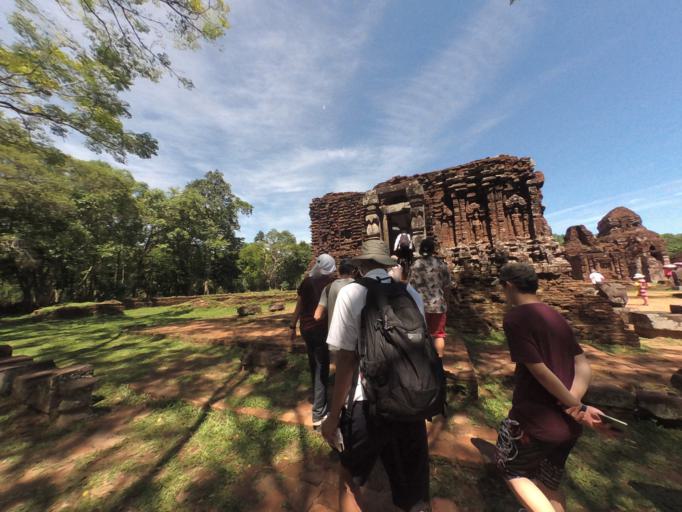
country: VN
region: Quang Nam
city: Dai Loc
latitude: 15.7629
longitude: 108.1244
